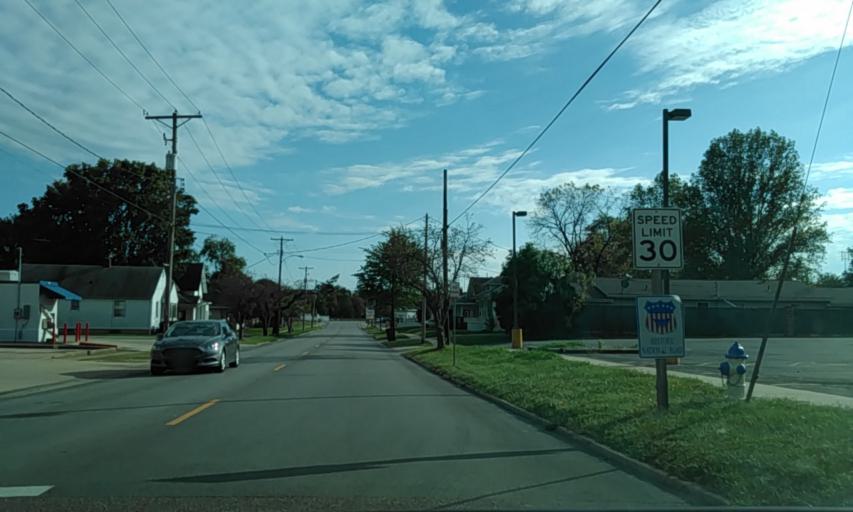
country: US
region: Illinois
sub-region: Bond County
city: Greenville
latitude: 38.8871
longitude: -89.4134
